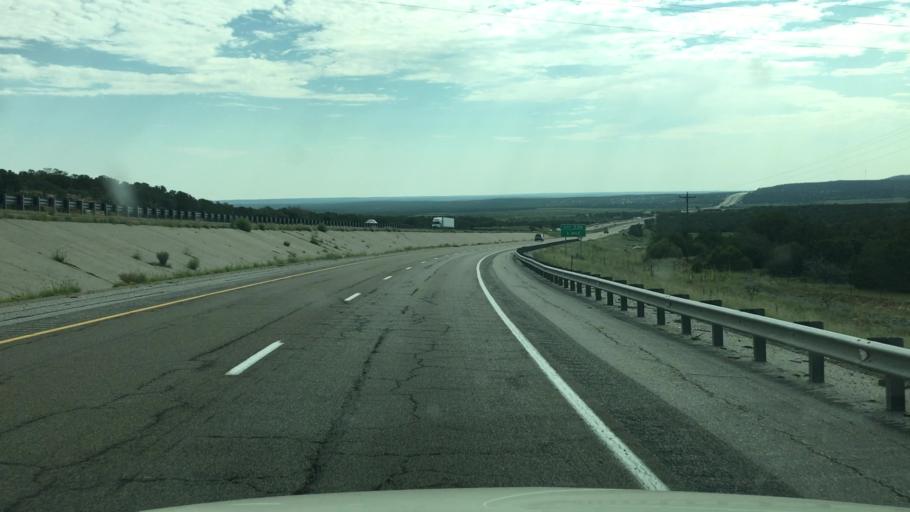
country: US
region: New Mexico
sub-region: Torrance County
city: Moriarty
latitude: 35.0054
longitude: -105.5425
